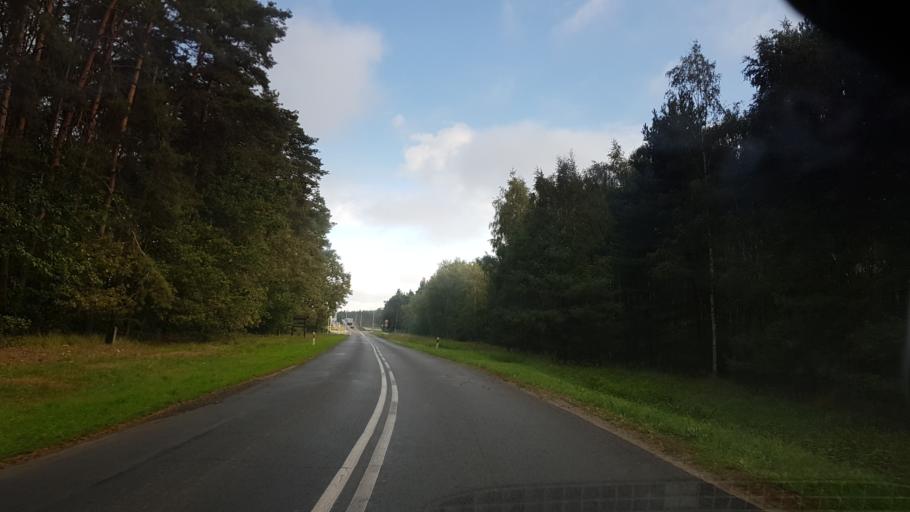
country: PL
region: Greater Poland Voivodeship
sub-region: Leszno
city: Leszno
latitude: 51.8021
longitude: 16.5816
